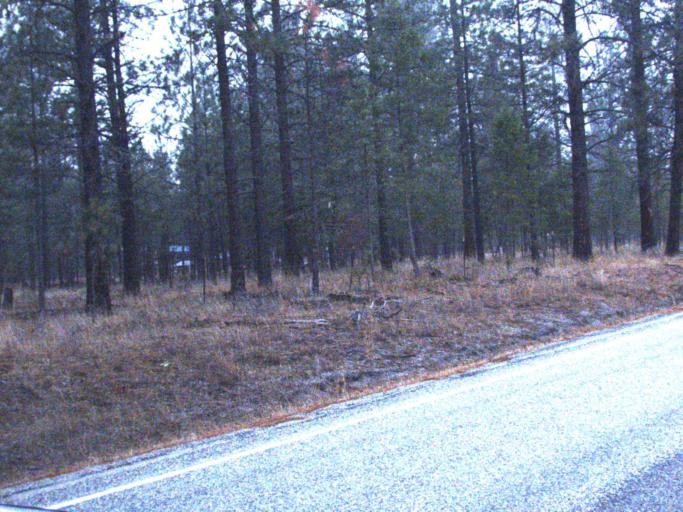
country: CA
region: British Columbia
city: Grand Forks
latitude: 48.9878
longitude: -118.2250
